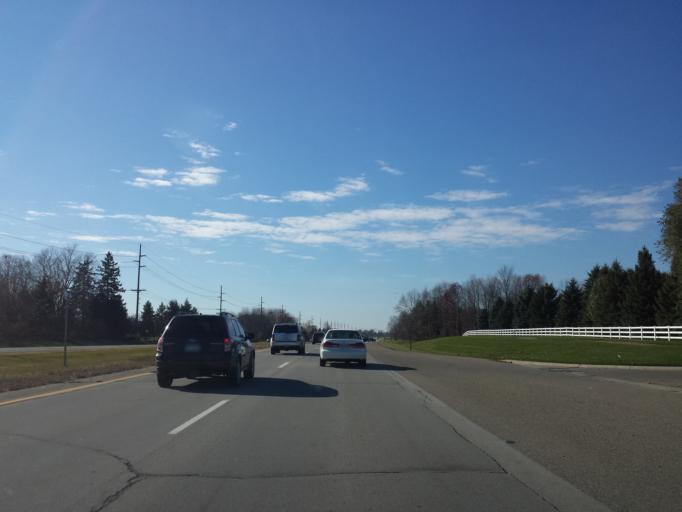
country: US
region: Michigan
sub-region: Oakland County
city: Milford
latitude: 42.6376
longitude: -83.6399
